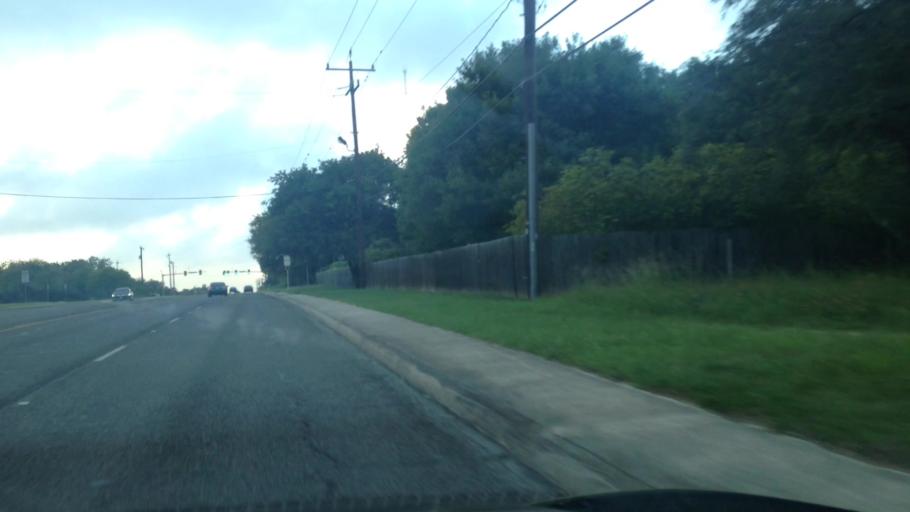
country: US
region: Texas
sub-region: Bexar County
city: Live Oak
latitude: 29.5956
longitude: -98.3830
